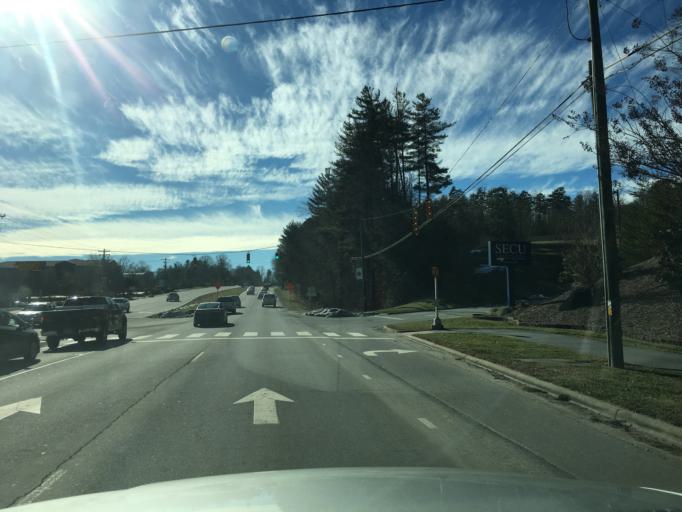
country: US
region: North Carolina
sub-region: Transylvania County
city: Brevard
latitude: 35.2725
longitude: -82.7058
